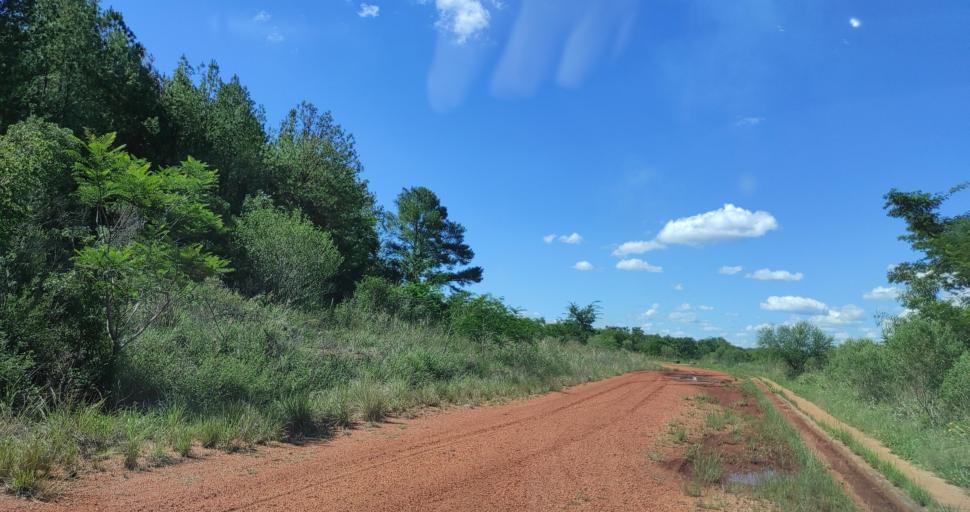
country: AR
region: Misiones
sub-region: Departamento de Candelaria
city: Candelaria
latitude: -27.4923
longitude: -55.7594
